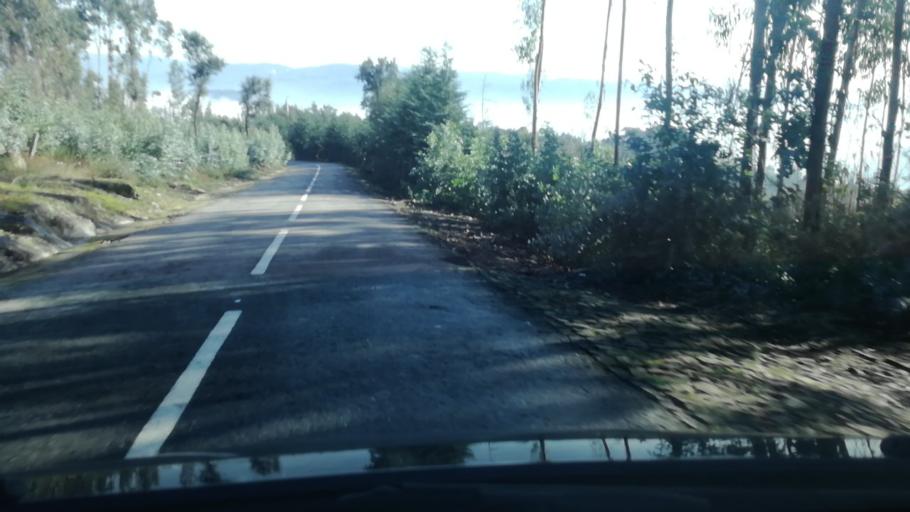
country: PT
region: Braga
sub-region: Guimaraes
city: Ponte
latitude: 41.5307
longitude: -8.3534
